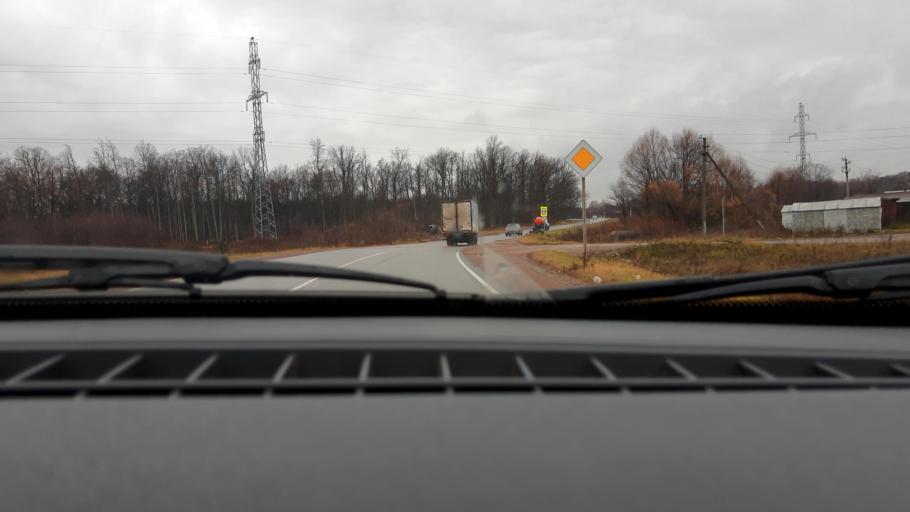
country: RU
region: Bashkortostan
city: Mikhaylovka
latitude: 54.8044
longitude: 55.8252
